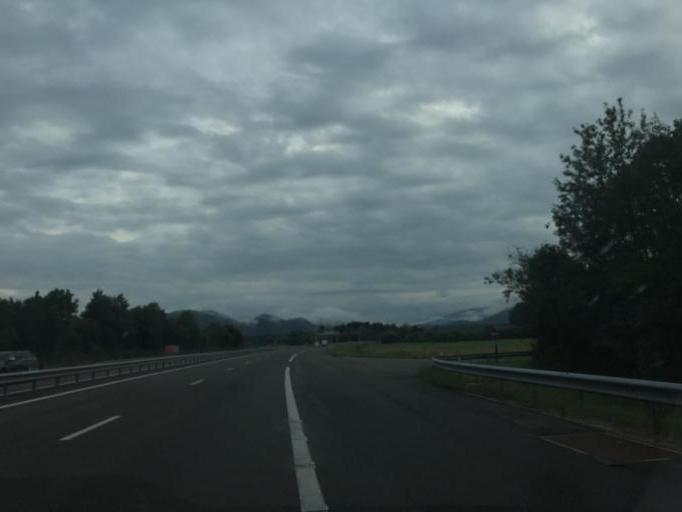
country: FR
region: Rhone-Alpes
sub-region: Departement de l'Ain
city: Saint-Martin-du-Frene
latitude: 46.1563
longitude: 5.5483
